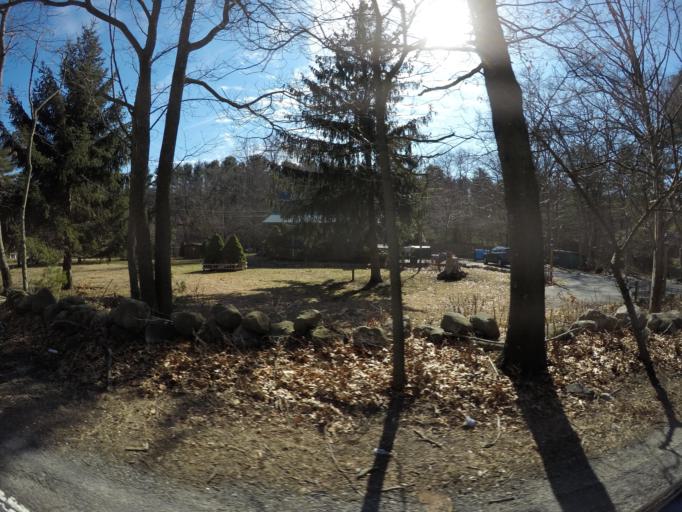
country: US
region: Massachusetts
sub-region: Bristol County
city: Easton
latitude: 42.0642
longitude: -71.1312
